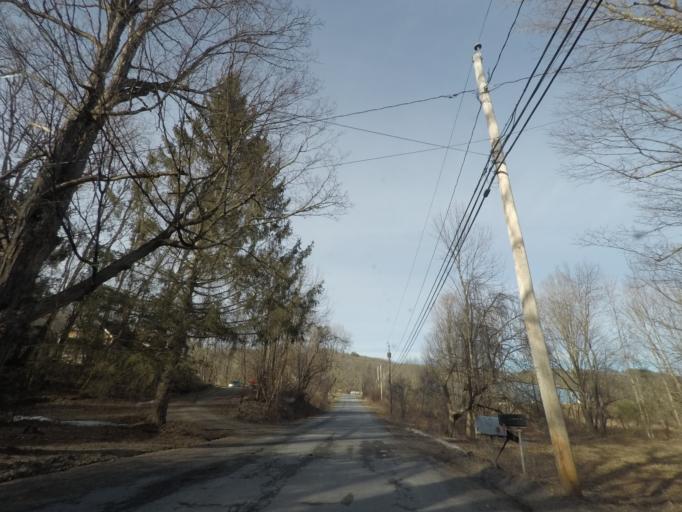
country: US
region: Massachusetts
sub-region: Berkshire County
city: Williamstown
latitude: 42.7378
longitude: -73.3625
